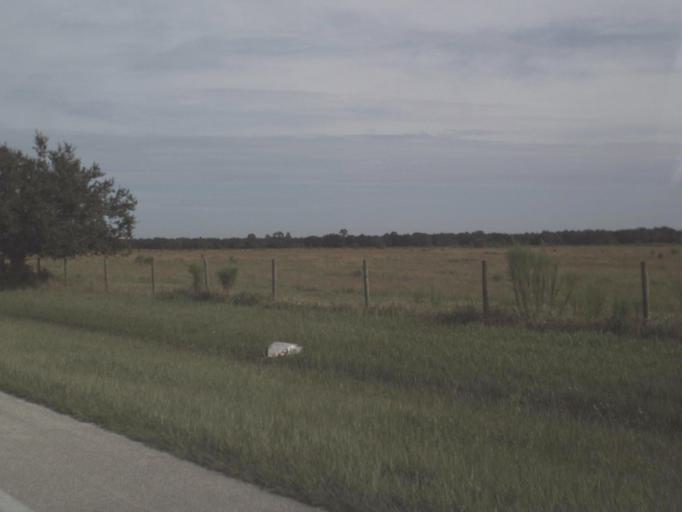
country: US
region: Florida
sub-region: DeSoto County
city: Nocatee
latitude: 27.0415
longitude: -81.7771
